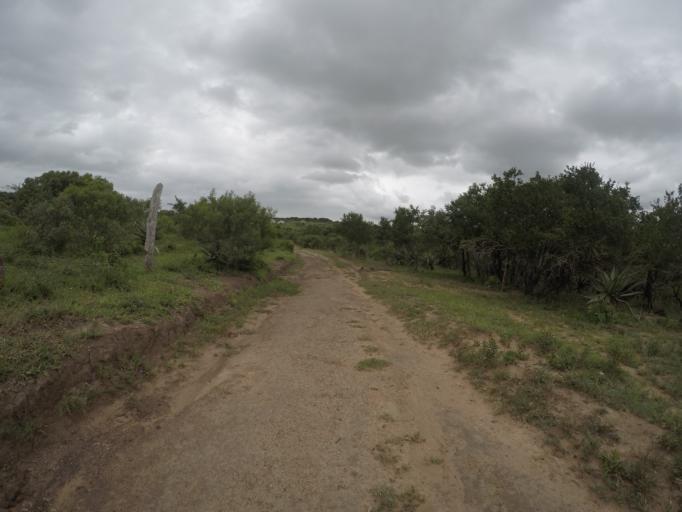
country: ZA
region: KwaZulu-Natal
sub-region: uThungulu District Municipality
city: Empangeni
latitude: -28.5956
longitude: 31.8479
